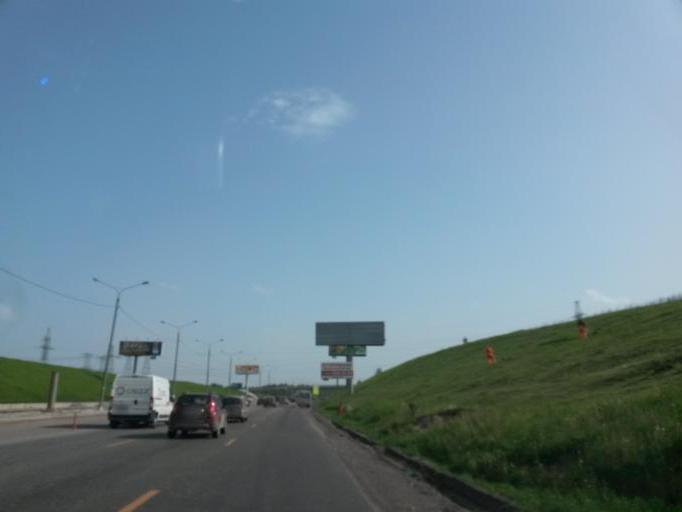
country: RU
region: Moscow
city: Annino
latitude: 55.5633
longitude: 37.6035
